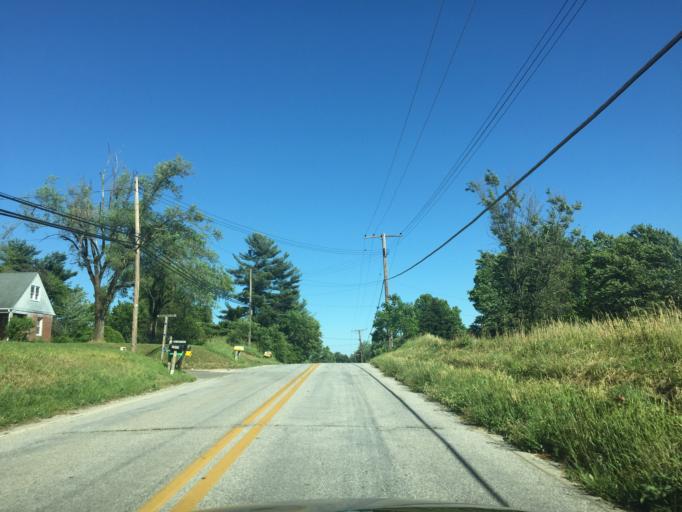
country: US
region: Maryland
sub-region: Carroll County
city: Westminster
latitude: 39.6005
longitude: -76.9419
